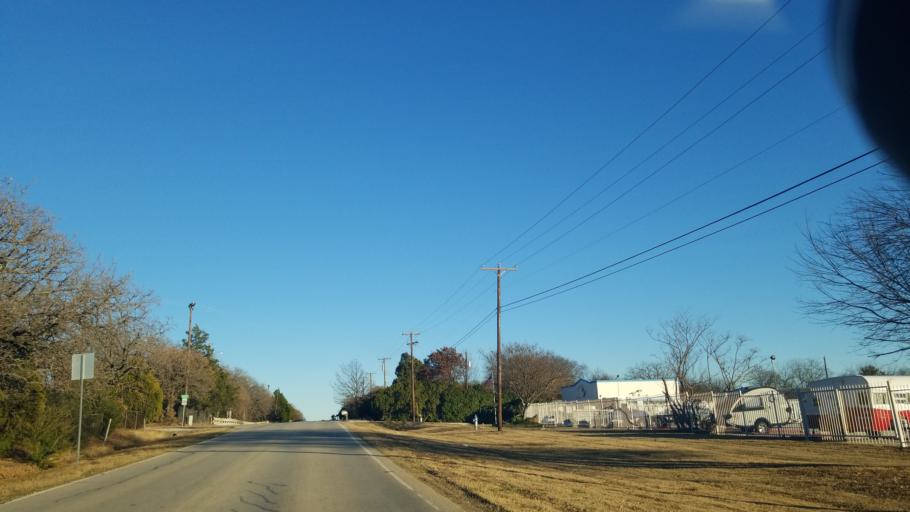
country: US
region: Texas
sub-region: Denton County
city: Corinth
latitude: 33.1631
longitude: -97.0656
